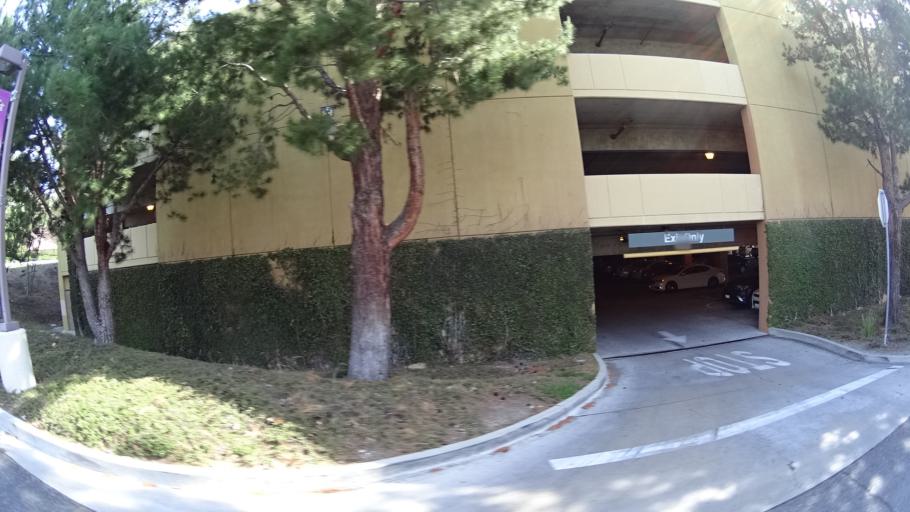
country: US
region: California
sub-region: Ventura County
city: Thousand Oaks
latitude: 34.1832
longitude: -118.8789
